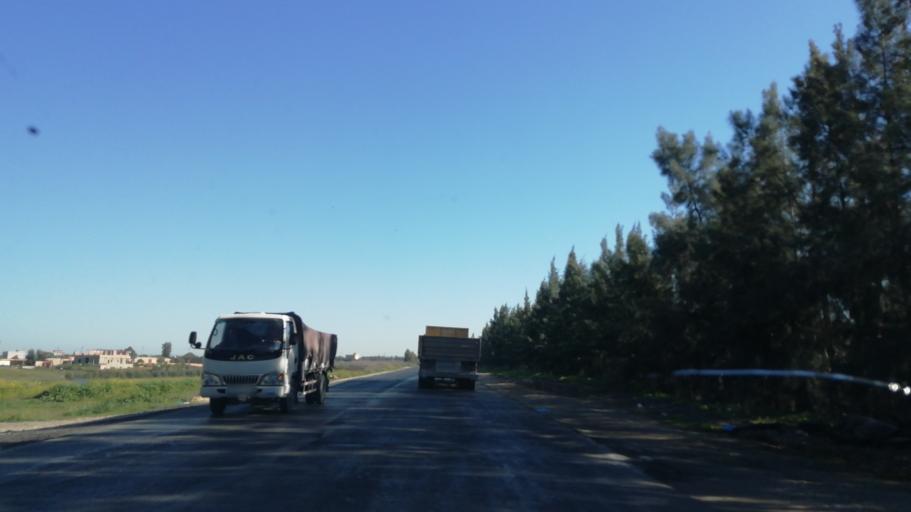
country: DZ
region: Relizane
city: Zemoura
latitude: 35.7576
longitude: 0.6688
